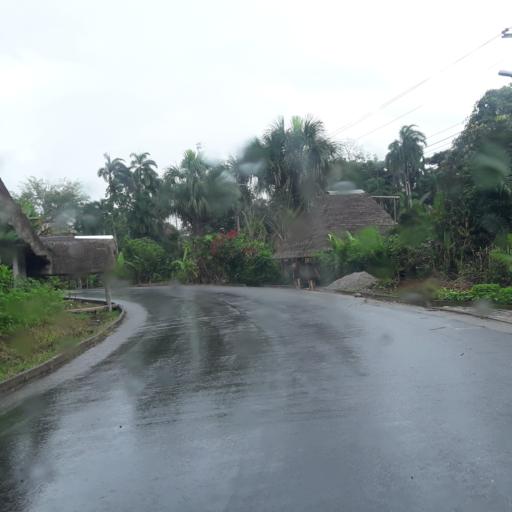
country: EC
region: Napo
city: Tena
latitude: -1.0383
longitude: -77.6641
